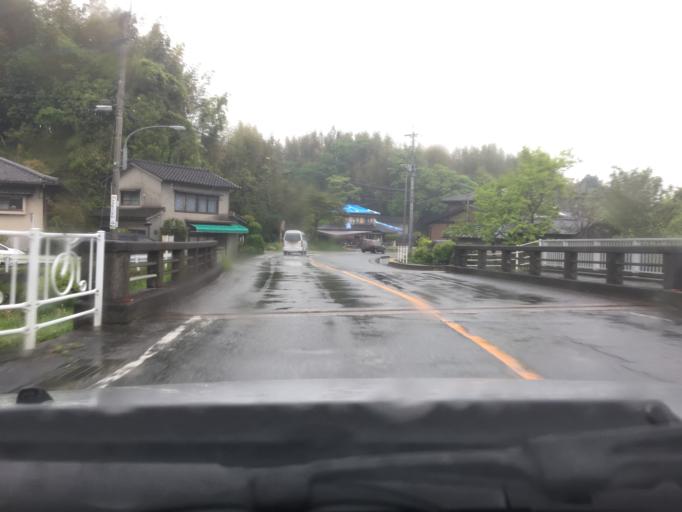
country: JP
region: Kumamoto
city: Ueki
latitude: 32.8628
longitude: 130.6869
